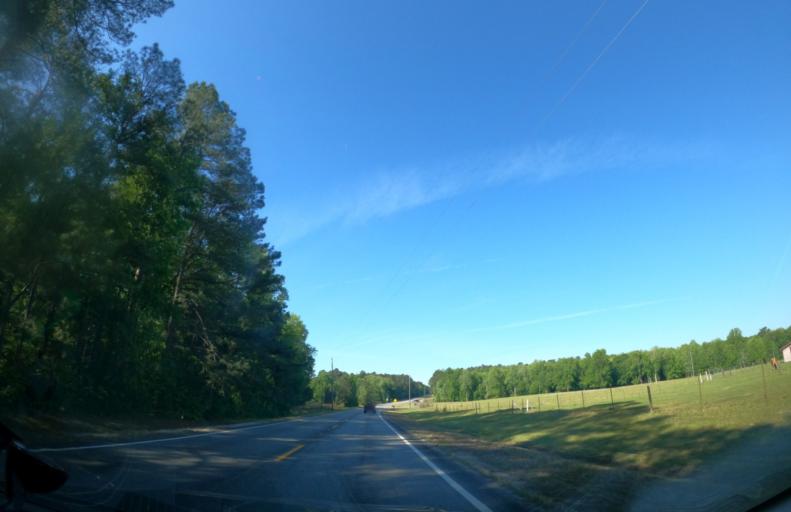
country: US
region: Georgia
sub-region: Columbia County
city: Harlem
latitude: 33.3433
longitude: -82.3514
